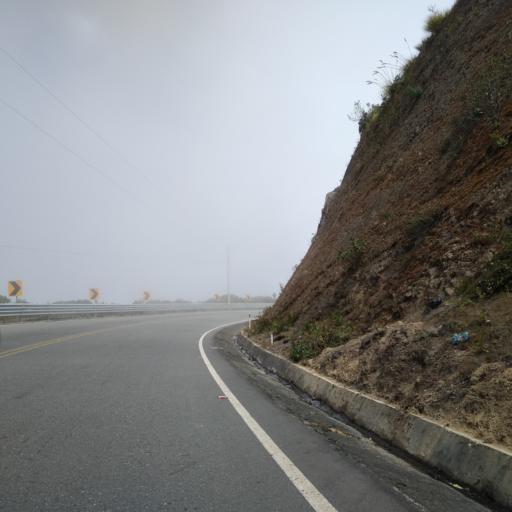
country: EC
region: Cotopaxi
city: La Mana
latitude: -0.9880
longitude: -78.9657
